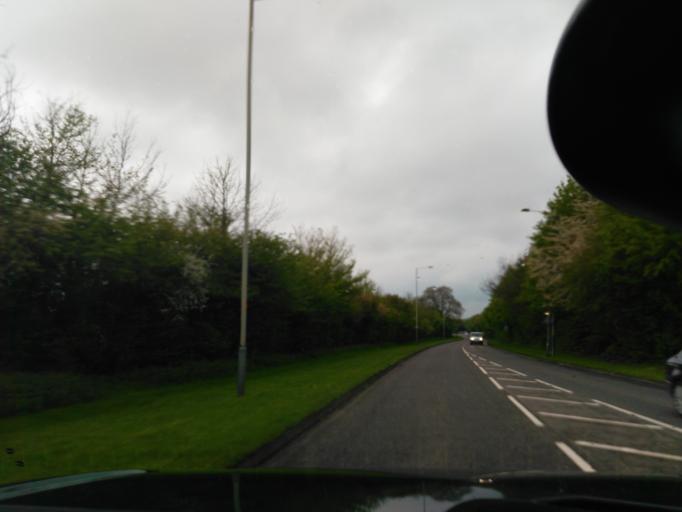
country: GB
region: England
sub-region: Wiltshire
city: Holt
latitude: 51.3284
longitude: -2.1739
